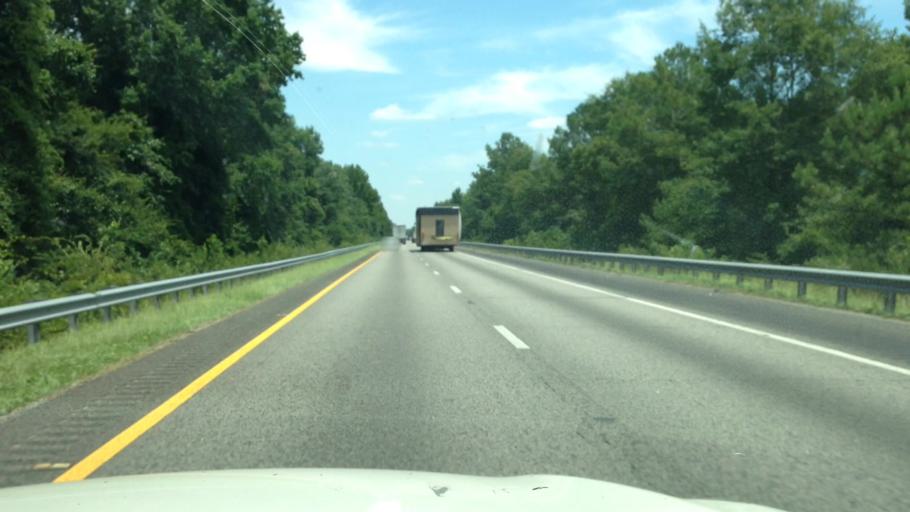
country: US
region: South Carolina
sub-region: Florence County
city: Florence
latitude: 34.2844
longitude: -79.6740
